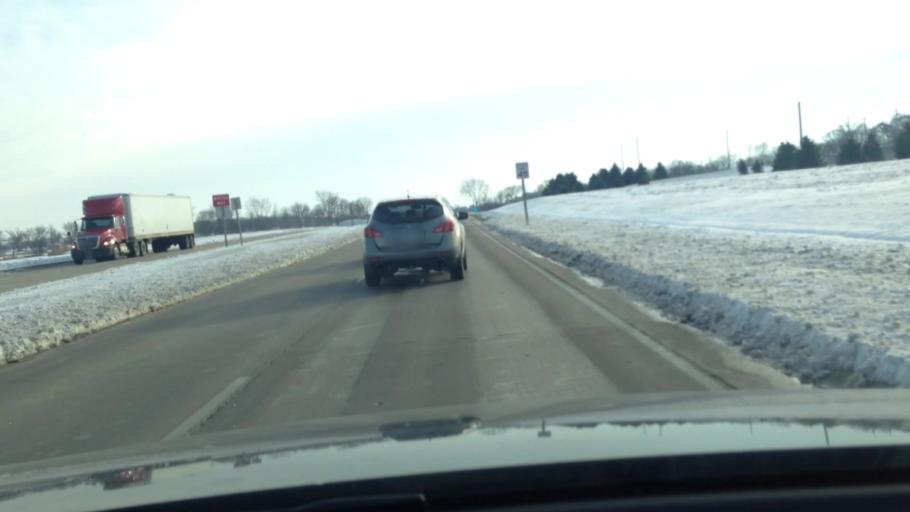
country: US
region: Wisconsin
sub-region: Walworth County
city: Lake Geneva
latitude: 42.5816
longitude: -88.4119
